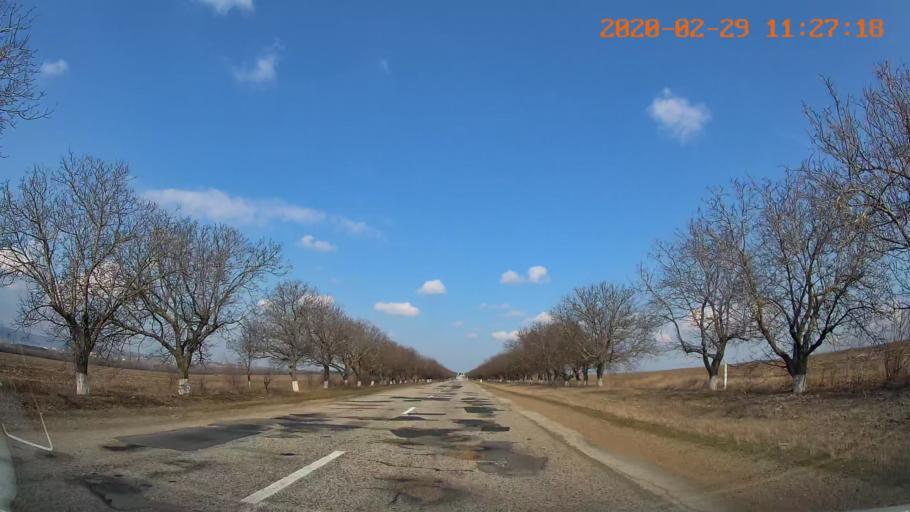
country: MD
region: Telenesti
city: Cocieri
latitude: 47.4661
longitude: 29.1431
